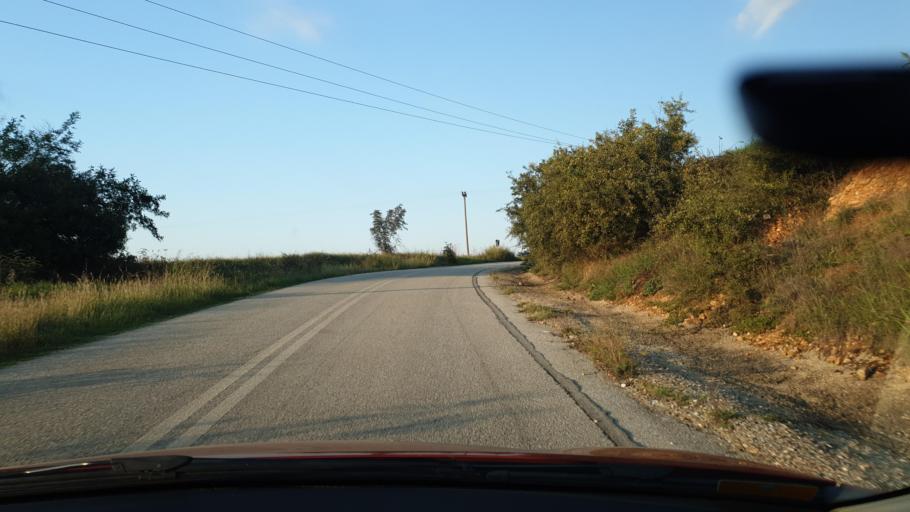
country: GR
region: Central Macedonia
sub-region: Nomos Thessalonikis
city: Nea Apollonia
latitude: 40.5553
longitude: 23.4523
